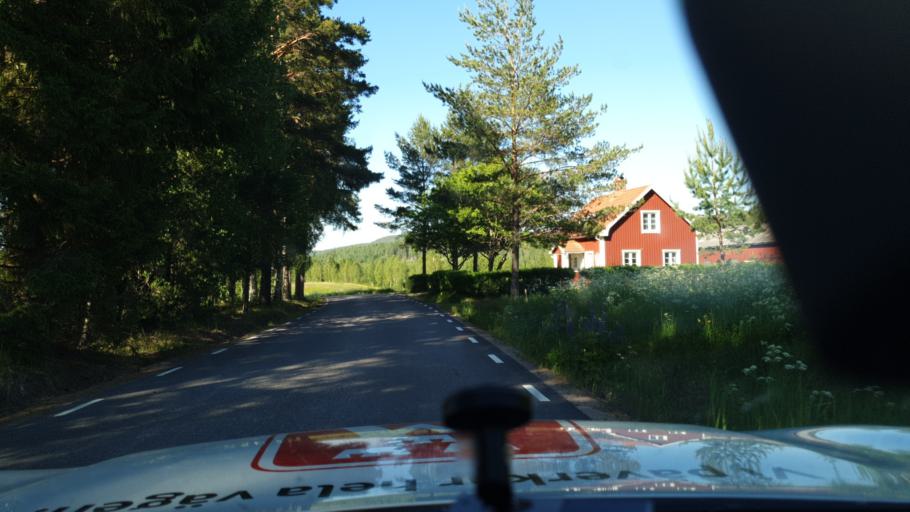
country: SE
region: Vaermland
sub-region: Torsby Kommun
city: Torsby
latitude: 60.1824
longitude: 13.0374
